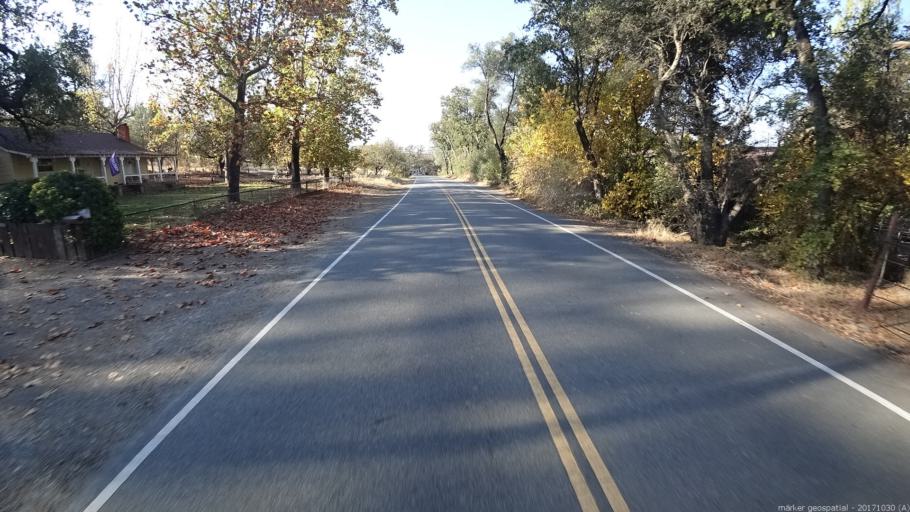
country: US
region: California
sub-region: Shasta County
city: Palo Cedro
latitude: 40.5502
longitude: -122.1710
